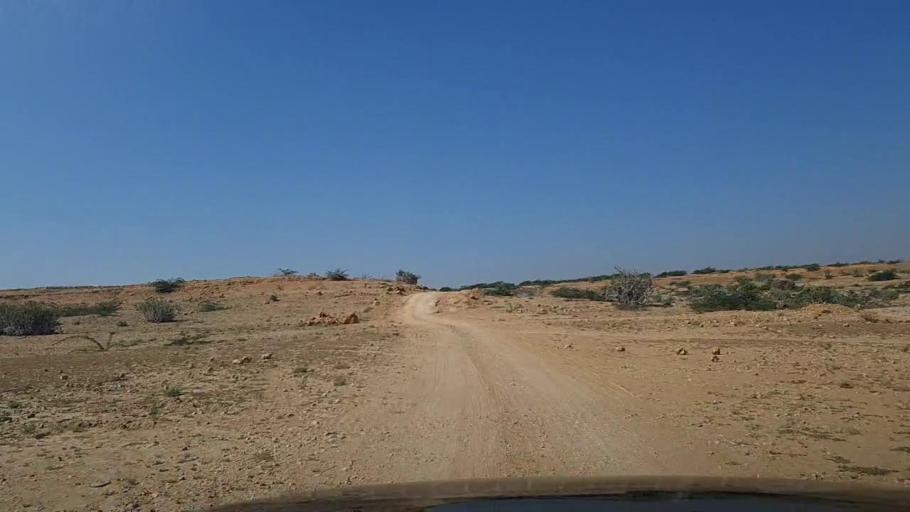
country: PK
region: Sindh
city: Thatta
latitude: 24.6268
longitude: 67.8589
